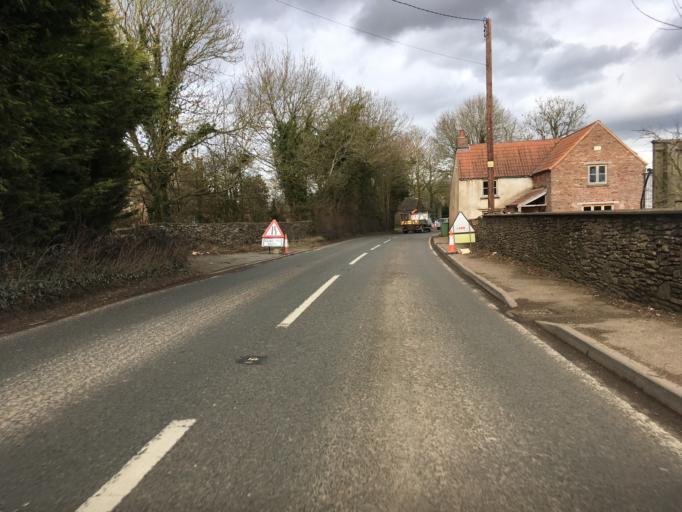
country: GB
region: England
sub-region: South Gloucestershire
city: Tytherington
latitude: 51.5547
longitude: -2.4667
